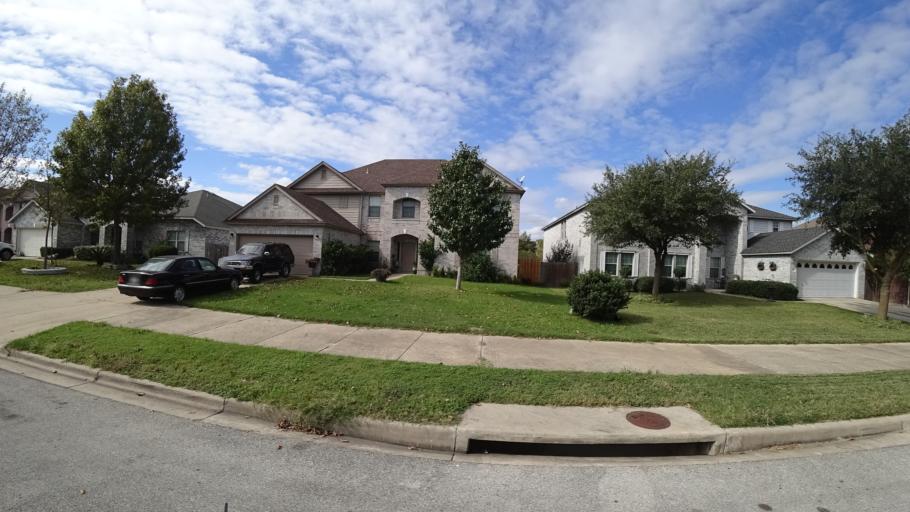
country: US
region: Texas
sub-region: Travis County
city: Pflugerville
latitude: 30.4478
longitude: -97.6271
